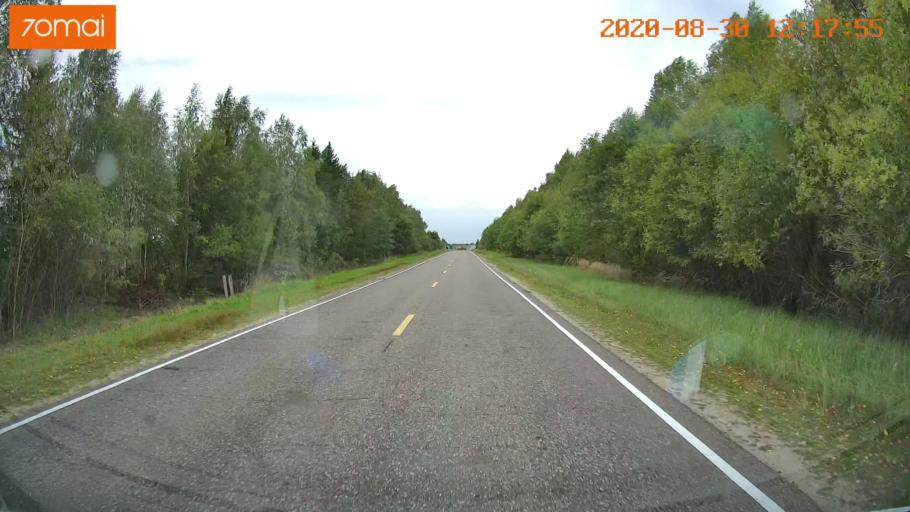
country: RU
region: Ivanovo
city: Yur'yevets
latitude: 57.3236
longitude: 42.9654
